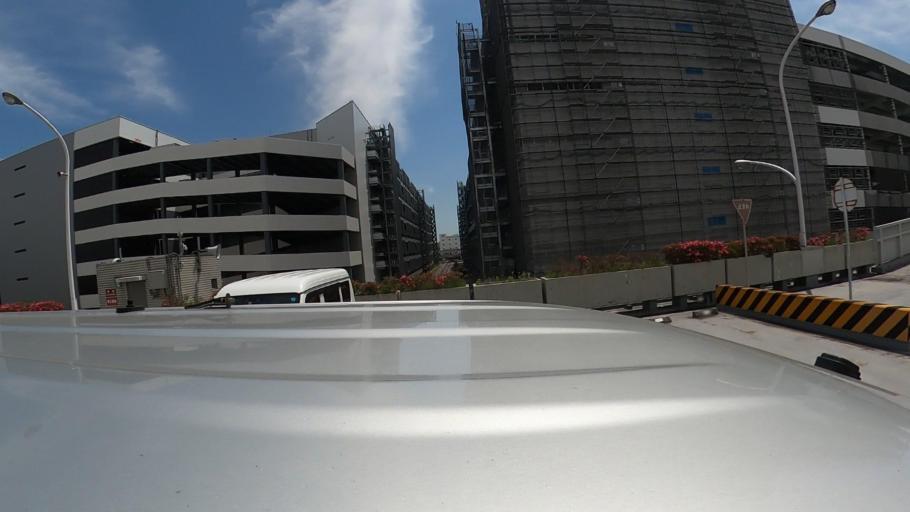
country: JP
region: Kanagawa
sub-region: Kawasaki-shi
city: Kawasaki
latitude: 35.5806
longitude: 139.7478
